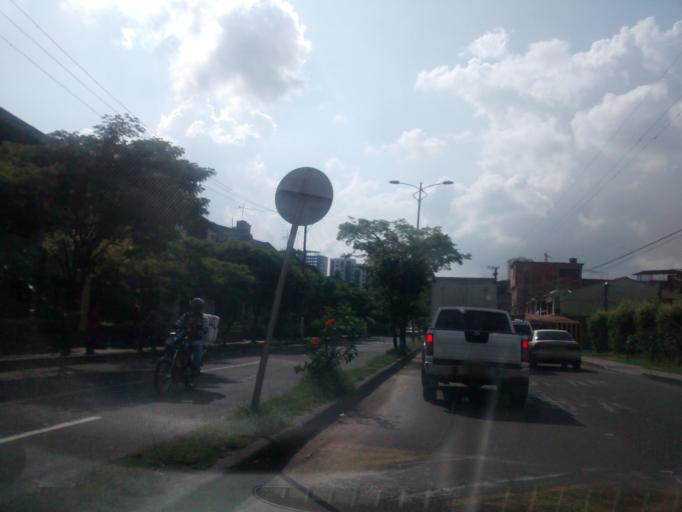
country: CO
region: Tolima
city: Ibague
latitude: 4.4423
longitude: -75.1981
